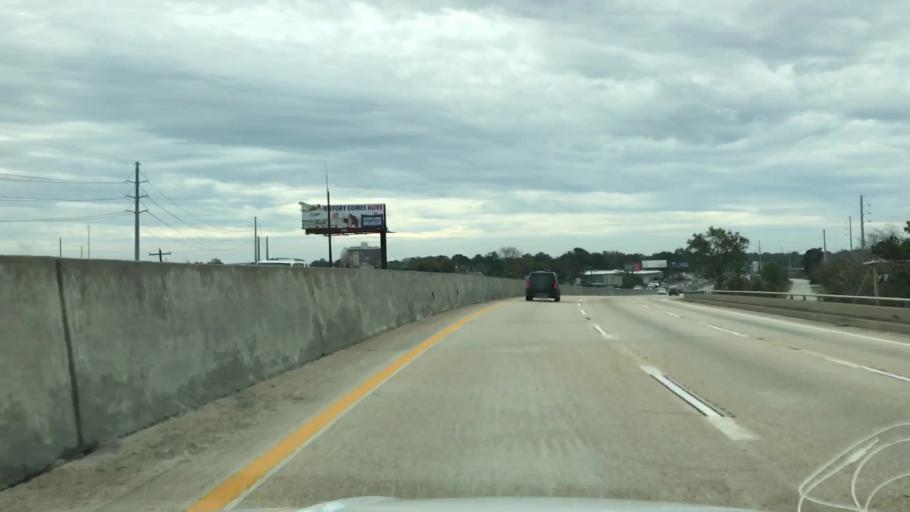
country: US
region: South Carolina
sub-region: Charleston County
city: North Charleston
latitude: 32.8239
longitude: -79.9533
